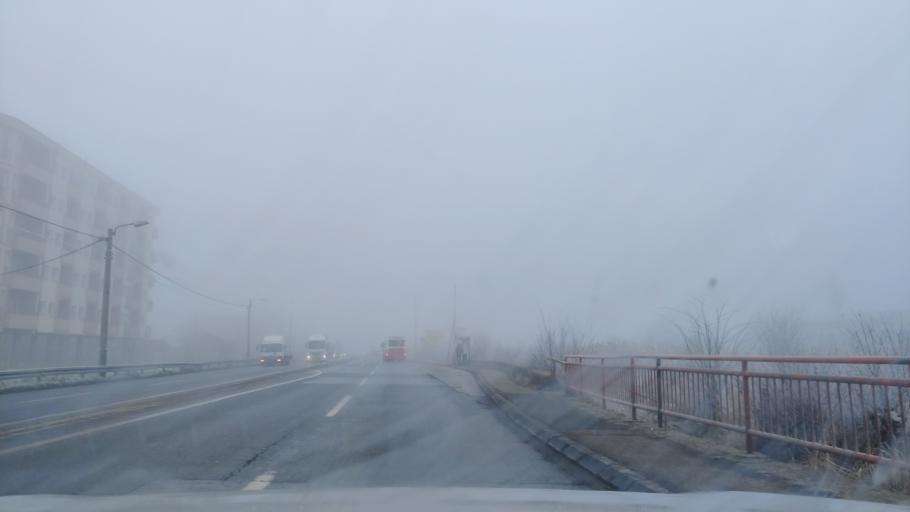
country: RS
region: Central Serbia
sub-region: Belgrade
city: Stari Grad
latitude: 44.8488
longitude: 20.4867
